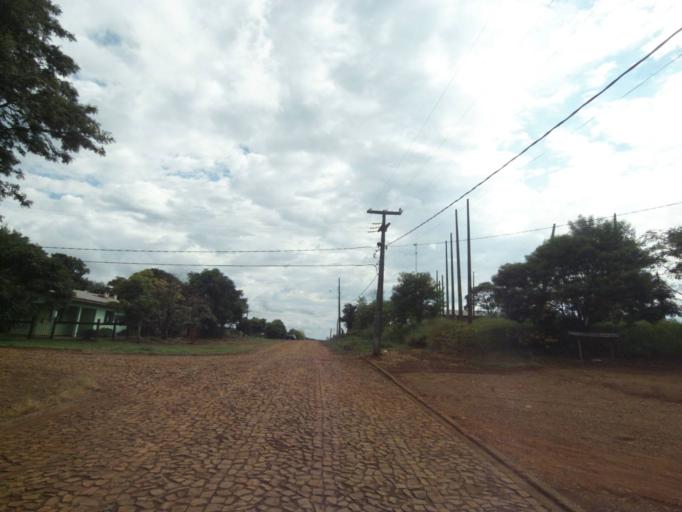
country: BR
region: Parana
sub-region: Pitanga
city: Pitanga
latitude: -24.9093
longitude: -52.0338
